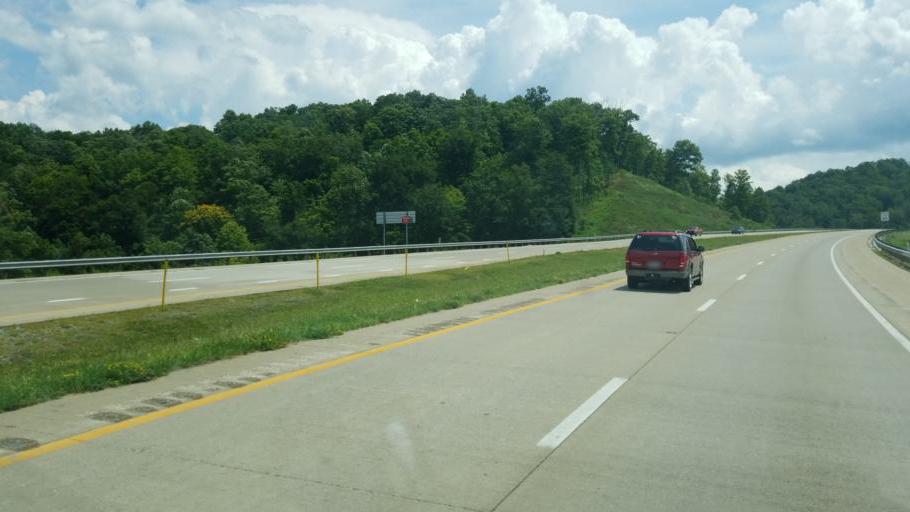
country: US
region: West Virginia
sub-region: Putnam County
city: Eleanor
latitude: 38.5228
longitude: -81.9345
